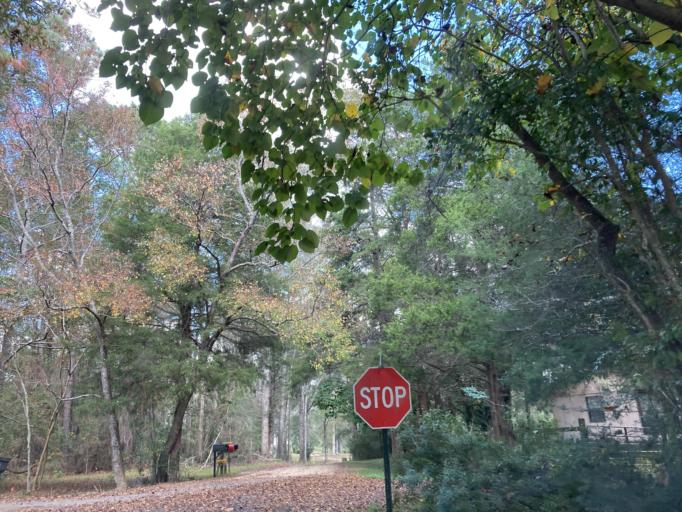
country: US
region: Mississippi
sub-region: Lamar County
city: Sumrall
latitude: 31.3744
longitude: -89.5441
